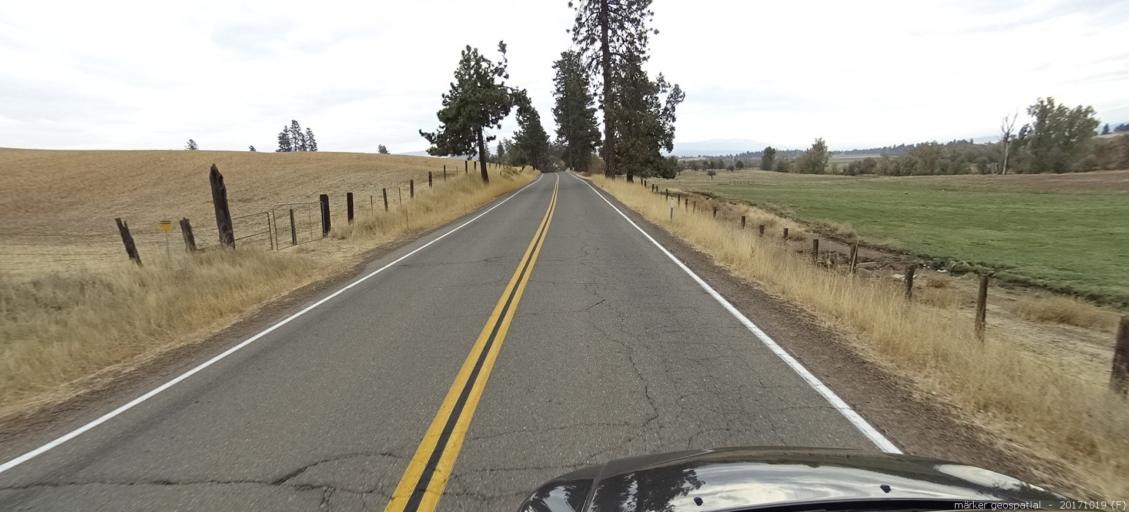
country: US
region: California
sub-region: Shasta County
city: Burney
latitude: 41.0530
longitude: -121.3548
